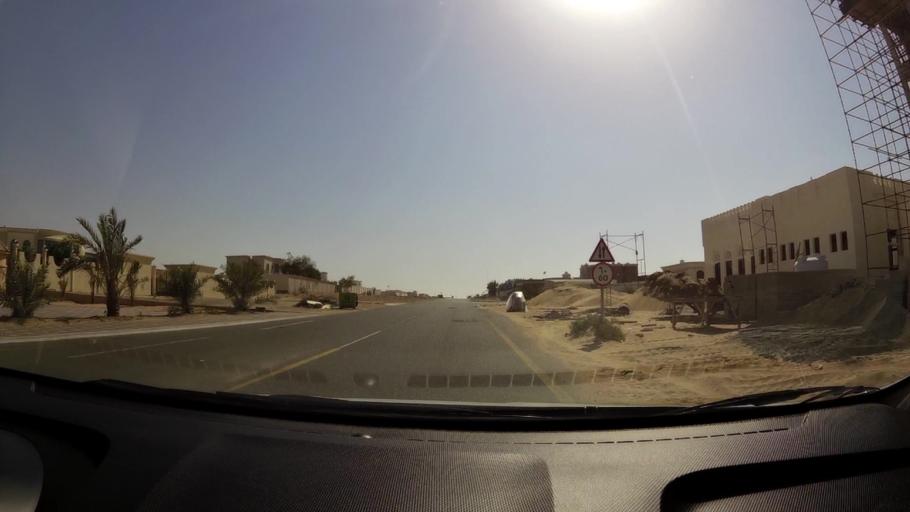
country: AE
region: Umm al Qaywayn
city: Umm al Qaywayn
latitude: 25.4964
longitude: 55.5969
